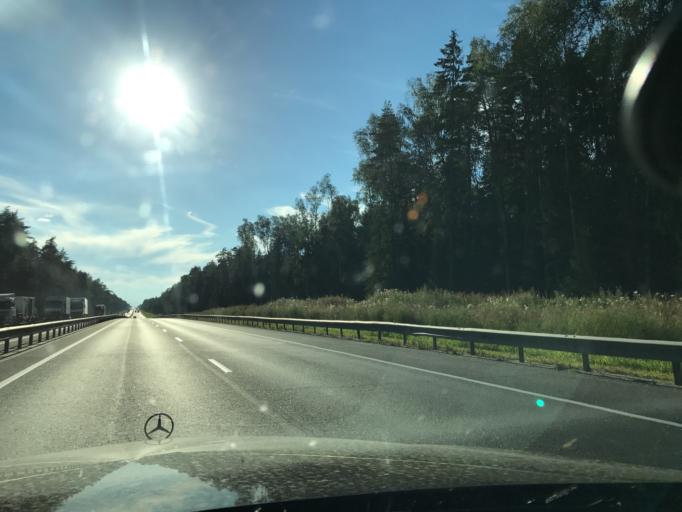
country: RU
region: Vladimir
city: Krasnyy Oktyabr'
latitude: 56.2209
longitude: 41.5147
